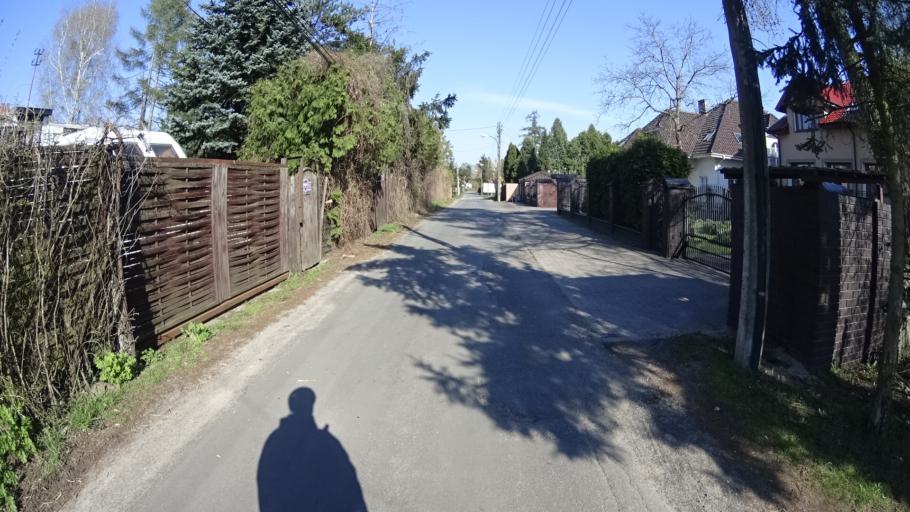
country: PL
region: Masovian Voivodeship
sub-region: Warszawa
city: Bemowo
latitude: 52.2470
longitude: 20.8880
